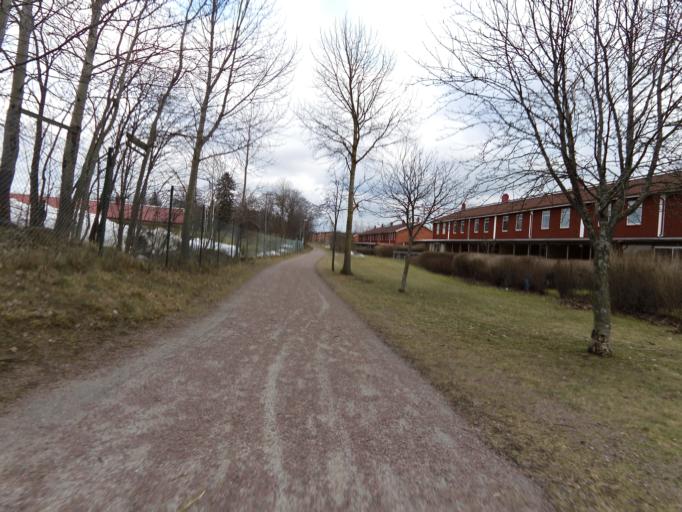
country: SE
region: Gaevleborg
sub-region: Gavle Kommun
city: Gavle
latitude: 60.6724
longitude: 17.1783
